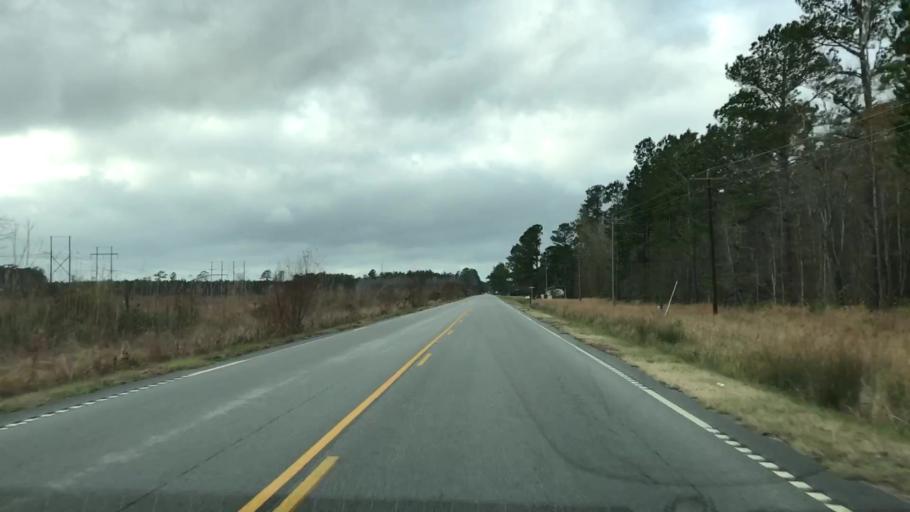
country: US
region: South Carolina
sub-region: Berkeley County
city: Saint Stephen
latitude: 33.2821
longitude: -79.7343
